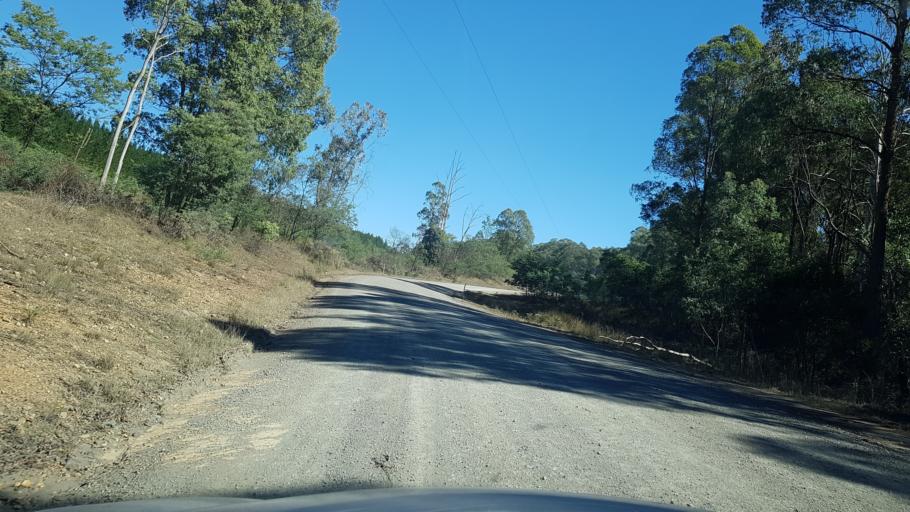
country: AU
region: Victoria
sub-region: Mansfield
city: Mansfield
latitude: -36.8529
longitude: 146.5226
